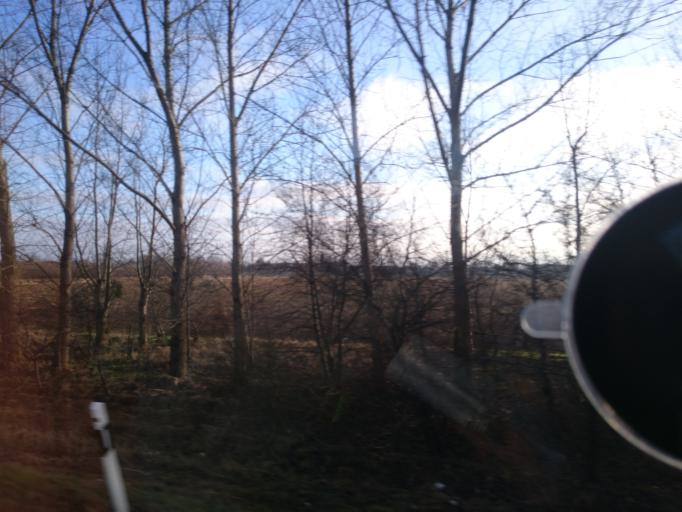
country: DE
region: Brandenburg
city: Fehrbellin
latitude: 52.7937
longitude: 12.7966
